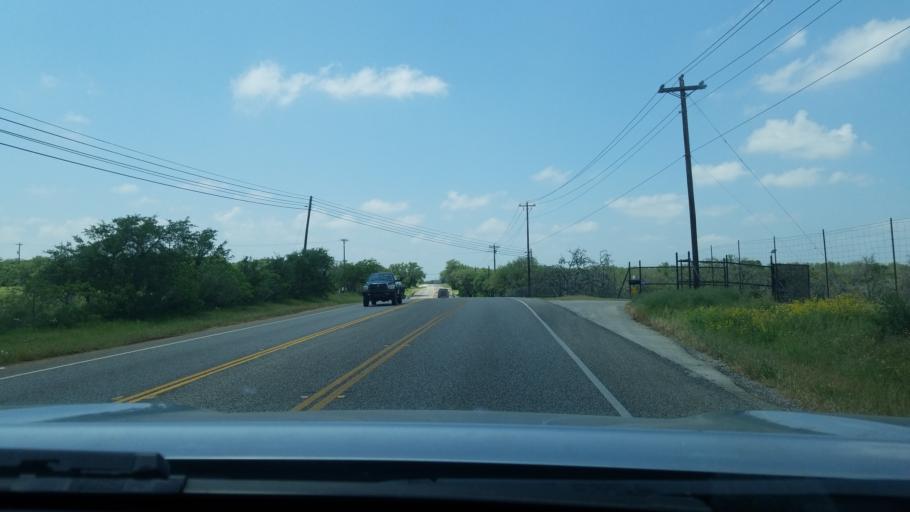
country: US
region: Texas
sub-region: Hays County
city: Woodcreek
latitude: 30.0200
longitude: -98.1517
